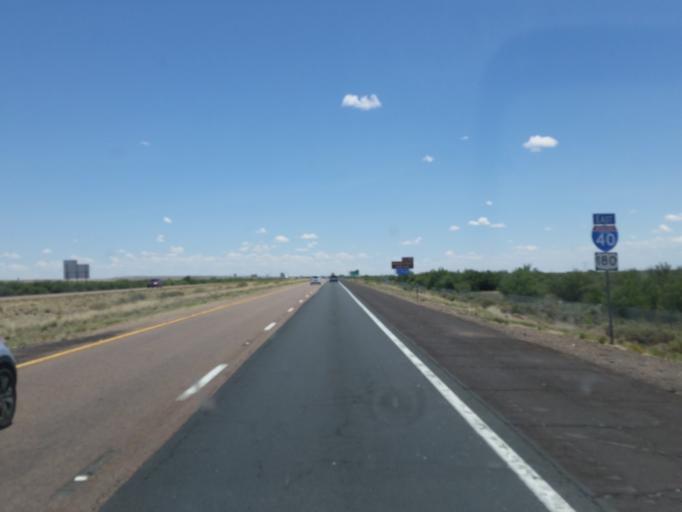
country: US
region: Arizona
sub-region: Navajo County
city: Winslow
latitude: 35.0144
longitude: -110.6625
